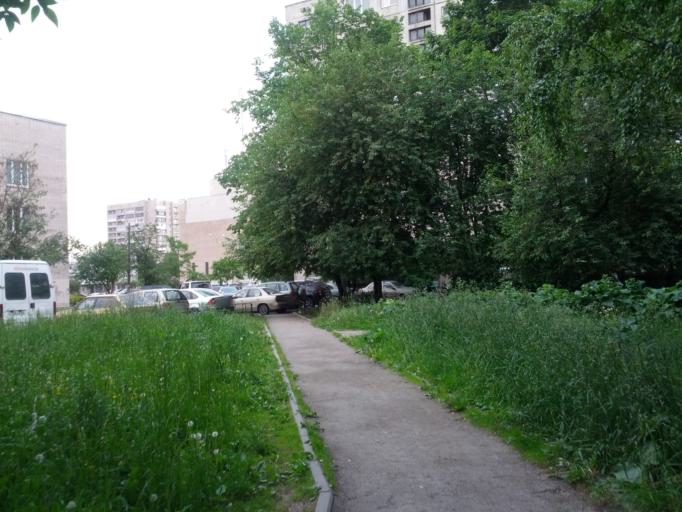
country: RU
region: St.-Petersburg
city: Obukhovo
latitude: 59.8942
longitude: 30.4758
